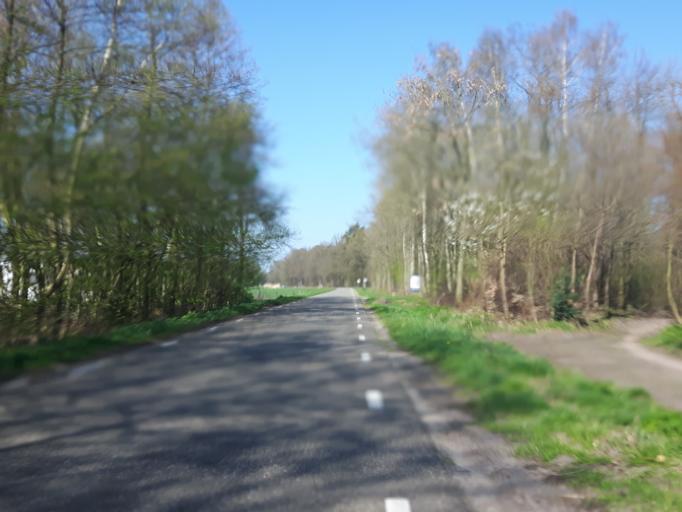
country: NL
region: Overijssel
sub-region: Gemeente Enschede
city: Enschede
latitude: 52.1713
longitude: 6.8376
